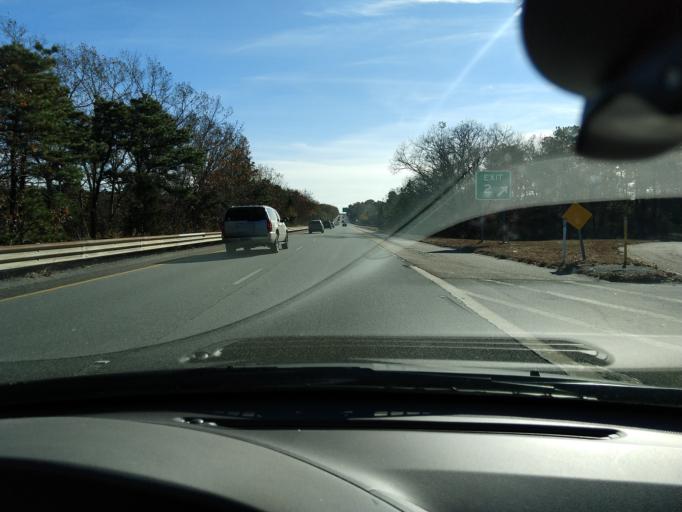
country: US
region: Massachusetts
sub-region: Barnstable County
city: Sagamore
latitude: 41.8122
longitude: -70.5532
